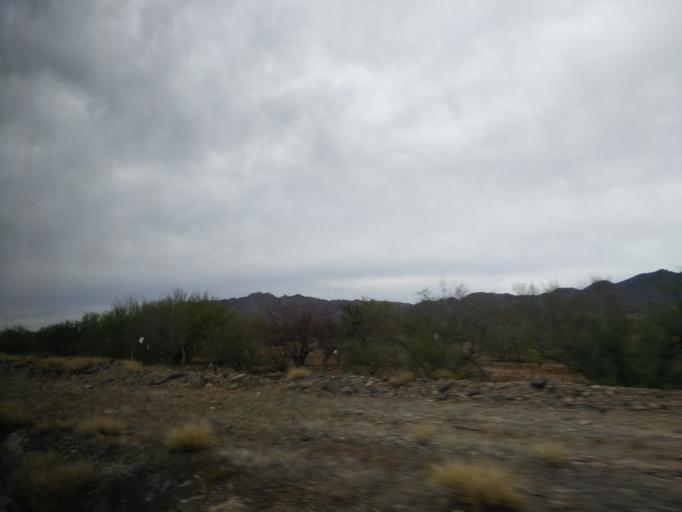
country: MX
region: Sonora
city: Hermosillo
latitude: 28.9442
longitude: -110.9618
